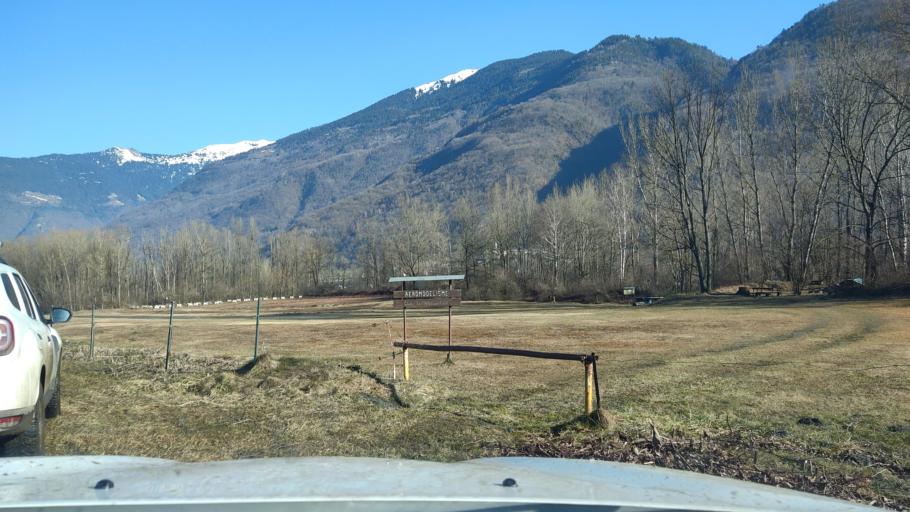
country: FR
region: Rhone-Alpes
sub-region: Departement de la Savoie
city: La Bathie
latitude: 45.6115
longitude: 6.4466
